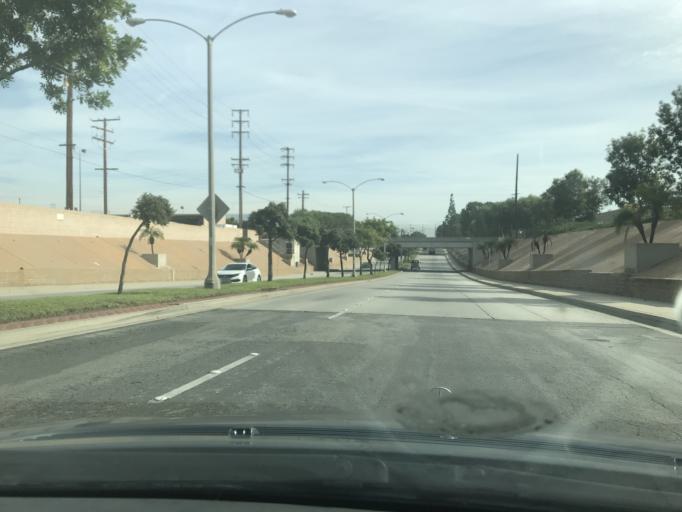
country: US
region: California
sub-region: Los Angeles County
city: Santa Fe Springs
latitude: 33.9354
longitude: -118.0627
